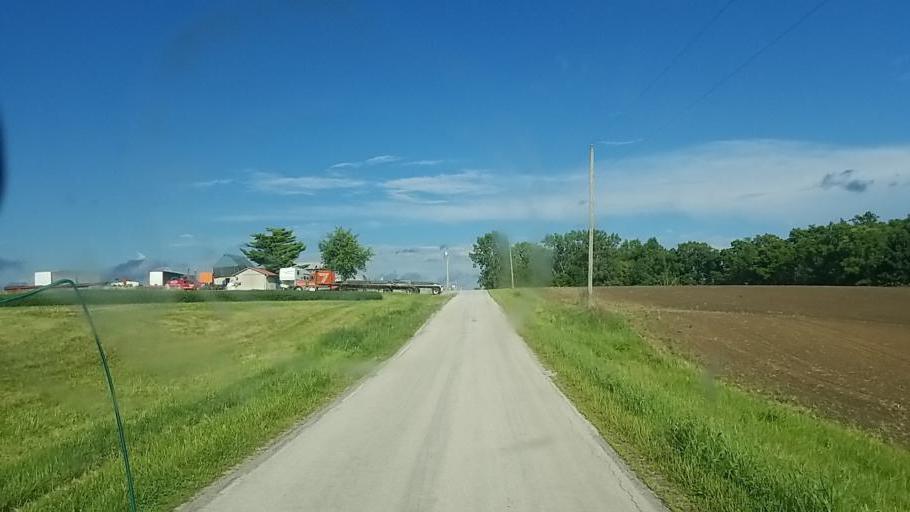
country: US
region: Ohio
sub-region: Wyandot County
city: Upper Sandusky
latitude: 40.7592
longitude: -83.3660
